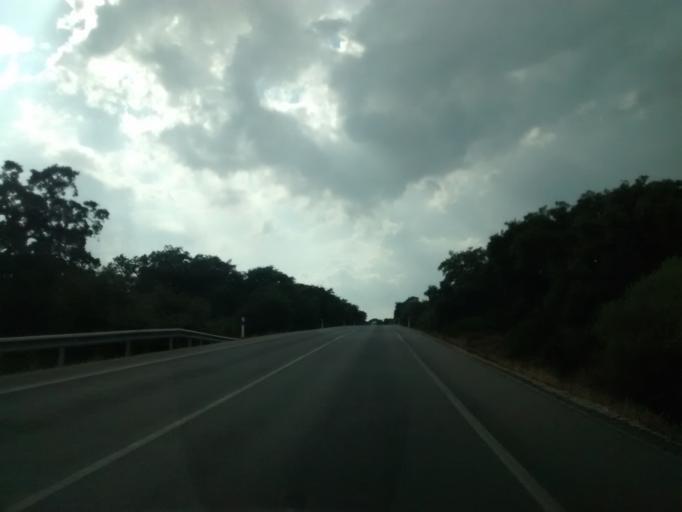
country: ES
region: Andalusia
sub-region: Provincia de Cadiz
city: Bornos
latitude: 36.7550
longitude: -5.7001
